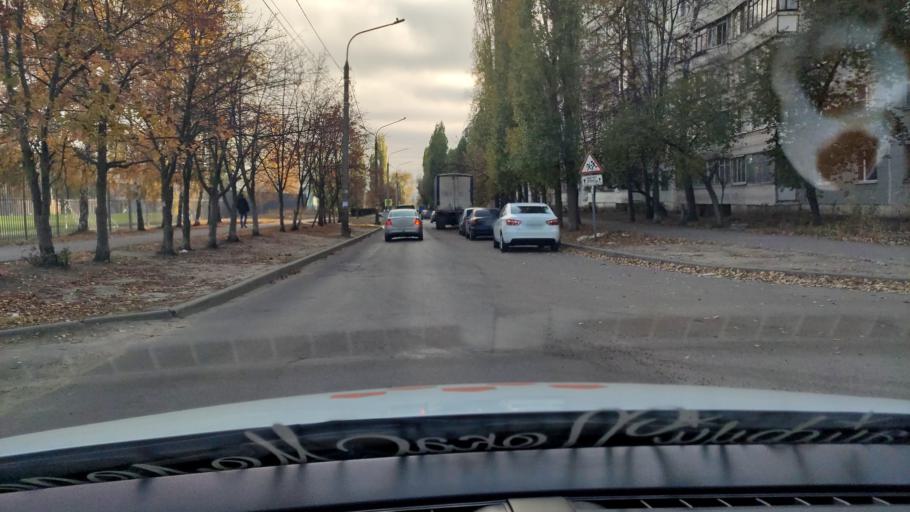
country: RU
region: Voronezj
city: Podgornoye
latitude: 51.7045
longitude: 39.1589
